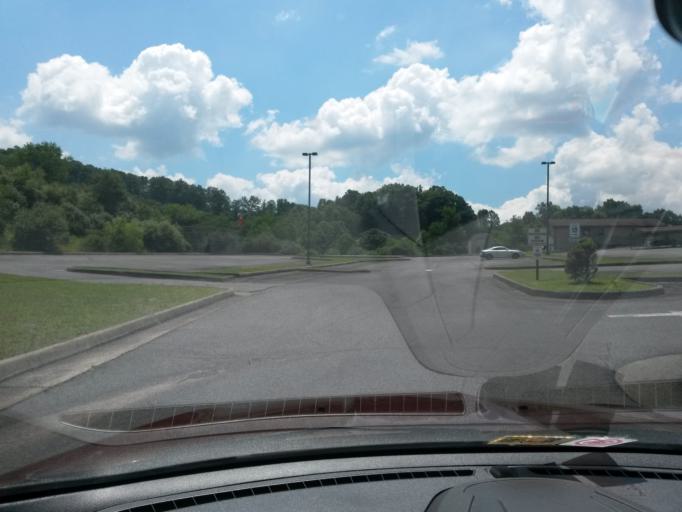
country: US
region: West Virginia
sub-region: Wyoming County
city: Mullens
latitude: 37.6417
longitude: -81.4547
